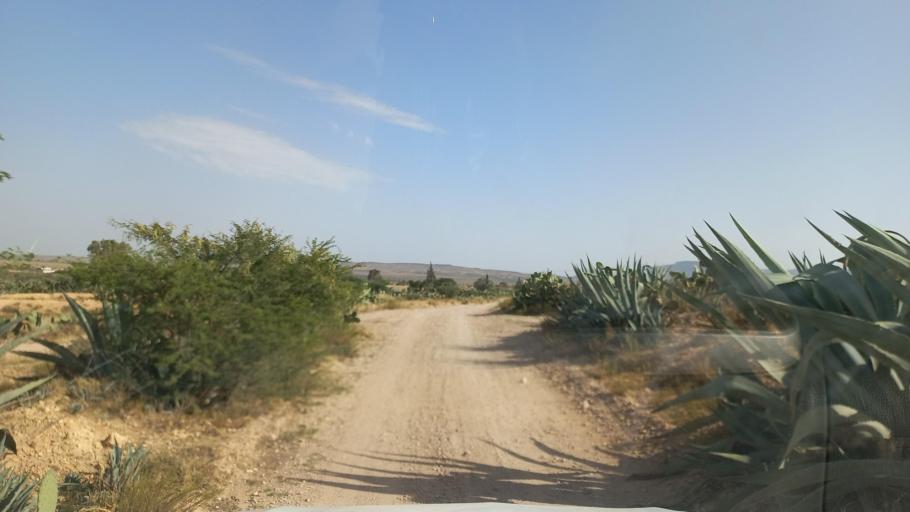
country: TN
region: Al Qasrayn
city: Kasserine
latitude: 35.2547
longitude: 8.9276
